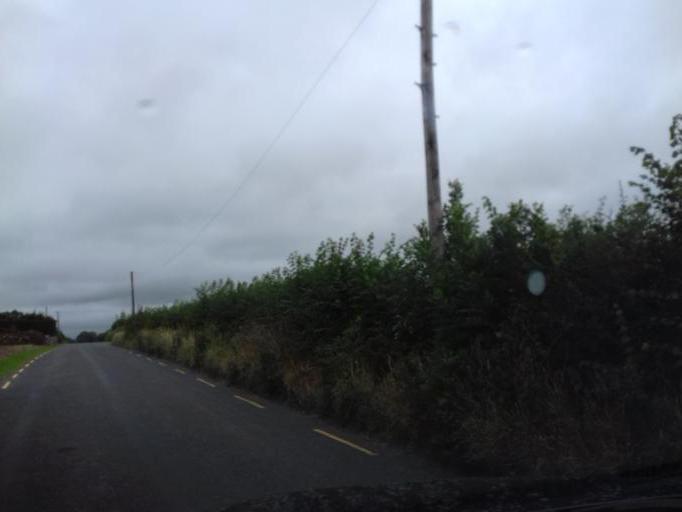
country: IE
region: Leinster
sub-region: Kilkenny
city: Graiguenamanagh
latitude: 52.6128
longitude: -7.0321
